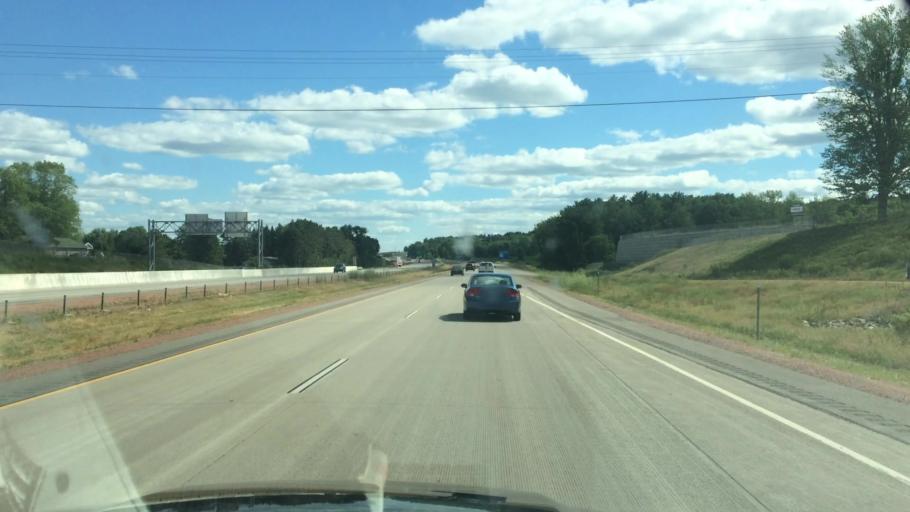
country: US
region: Wisconsin
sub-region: Marathon County
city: Wausau
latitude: 44.9850
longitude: -89.6570
